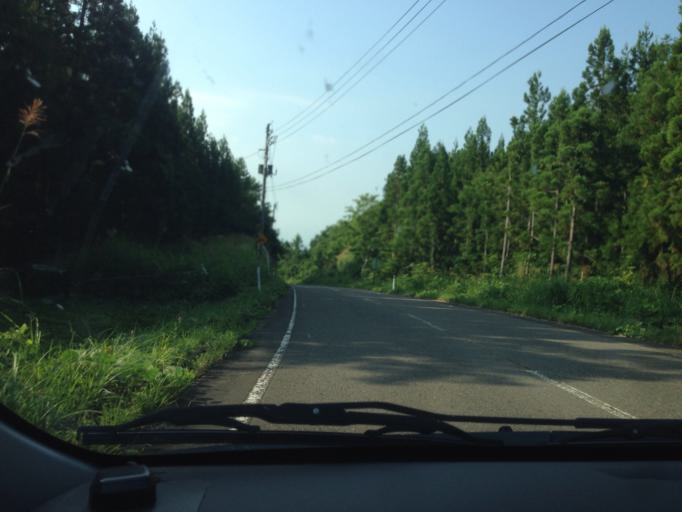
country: JP
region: Fukushima
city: Kitakata
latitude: 37.7433
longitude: 139.8684
